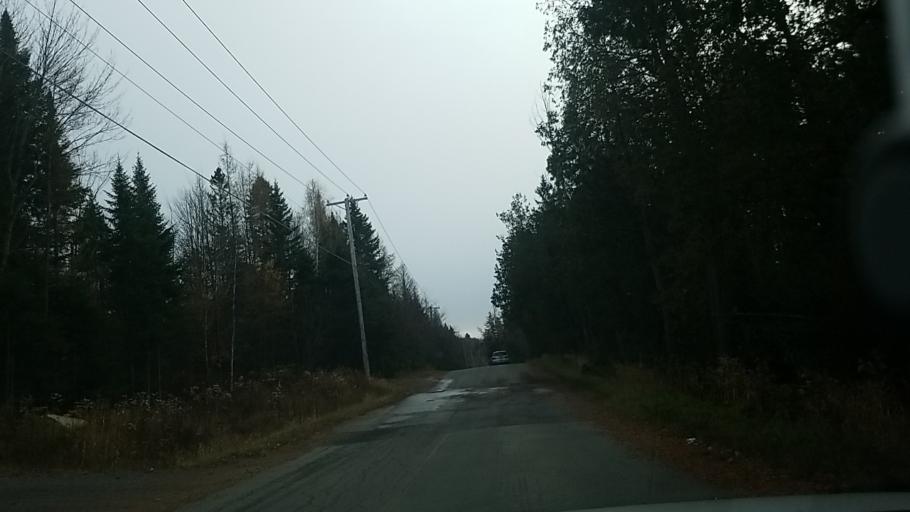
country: CA
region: Quebec
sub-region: Laurentides
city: Saint-Sauveur
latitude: 45.8203
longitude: -74.2486
